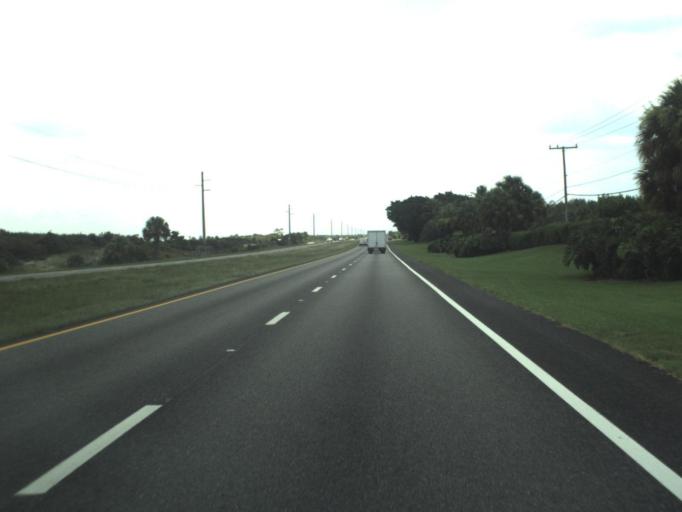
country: US
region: Florida
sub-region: Palm Beach County
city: Tequesta
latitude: 26.9919
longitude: -80.0950
